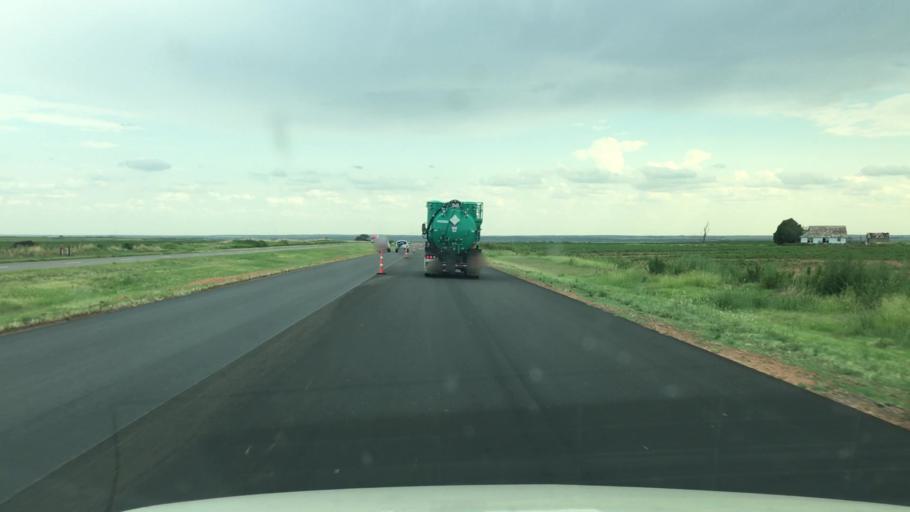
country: US
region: Texas
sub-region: Hall County
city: Memphis
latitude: 34.6170
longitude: -100.4710
